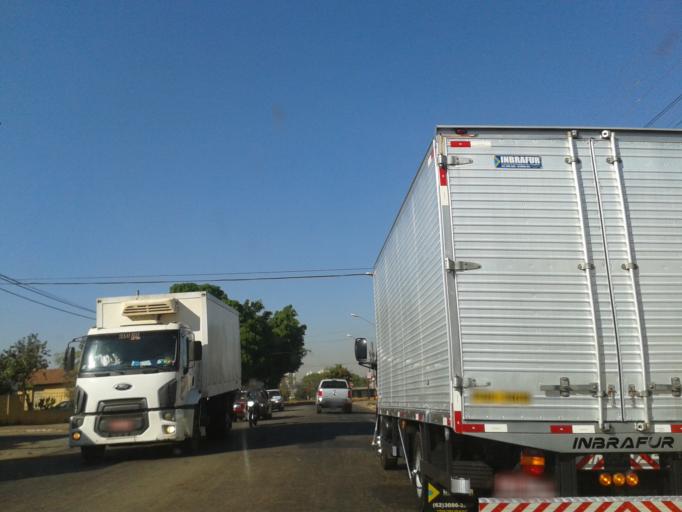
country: BR
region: Goias
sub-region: Goiania
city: Goiania
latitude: -16.6859
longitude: -49.3283
